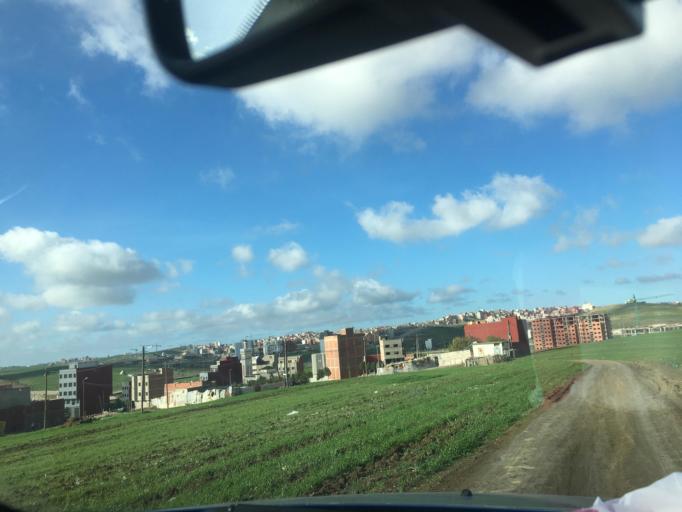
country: MA
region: Tanger-Tetouan
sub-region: Tanger-Assilah
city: Tangier
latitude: 35.7182
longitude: -5.8178
